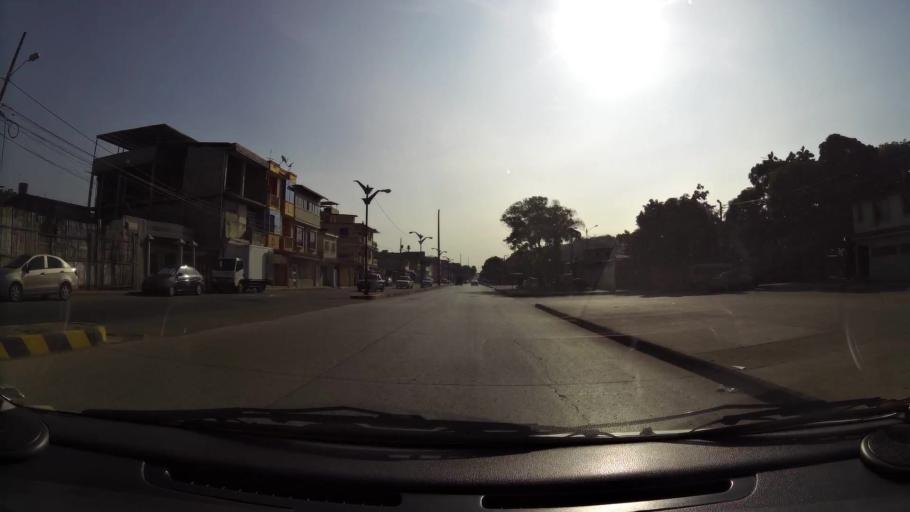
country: EC
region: Guayas
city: Eloy Alfaro
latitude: -2.1769
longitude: -79.8489
